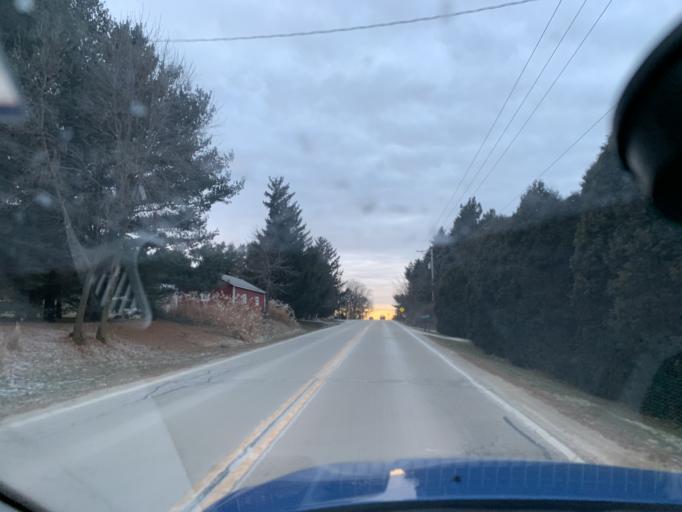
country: US
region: Wisconsin
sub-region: Dane County
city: Verona
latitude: 43.0457
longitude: -89.5489
